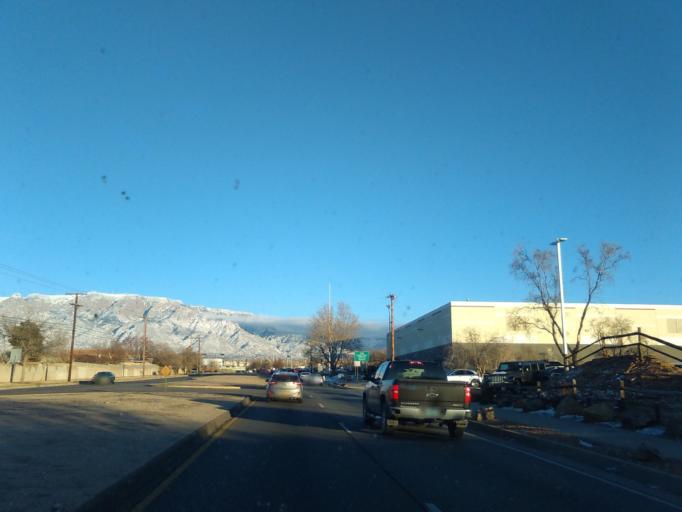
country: US
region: New Mexico
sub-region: Bernalillo County
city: North Valley
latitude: 35.1845
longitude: -106.5888
